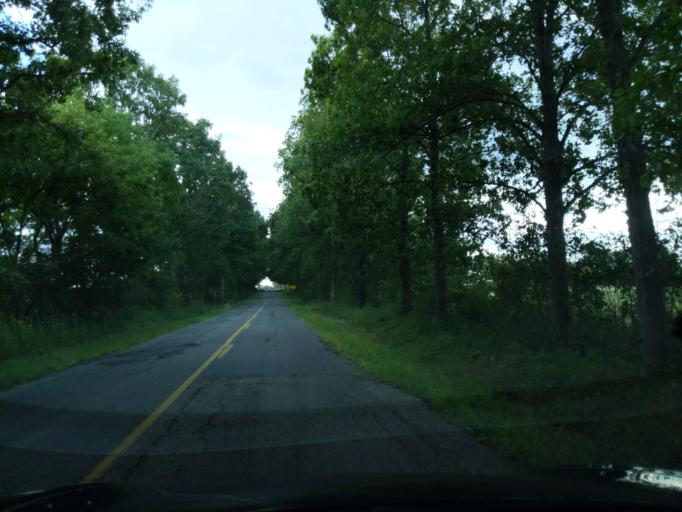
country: US
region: Michigan
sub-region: Eaton County
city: Eaton Rapids
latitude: 42.4464
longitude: -84.5803
